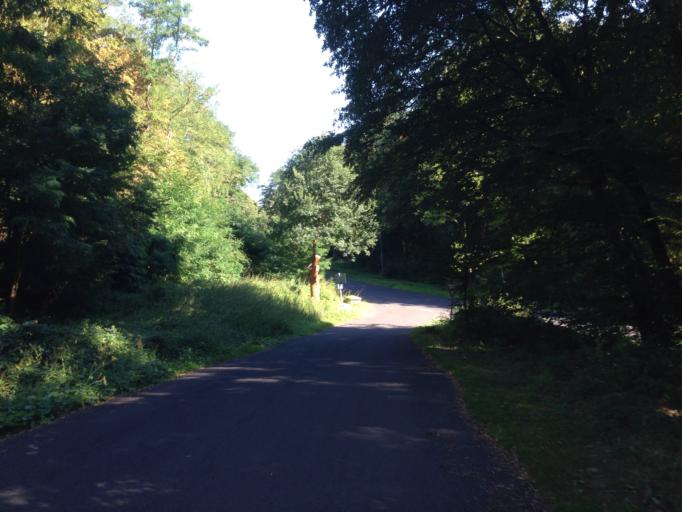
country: DE
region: Hesse
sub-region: Regierungsbezirk Giessen
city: Giessen
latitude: 50.5472
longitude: 8.7283
